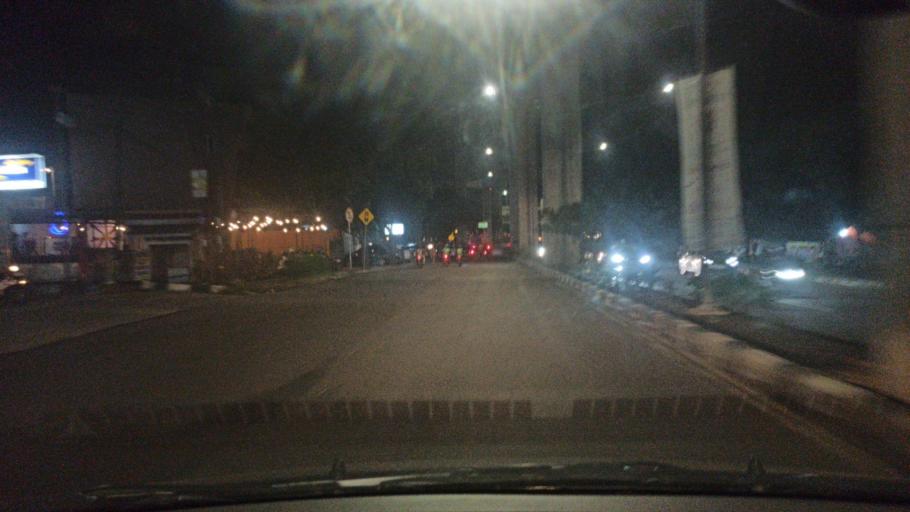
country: ID
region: South Sumatra
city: Palembang
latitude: -2.9631
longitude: 104.7364
